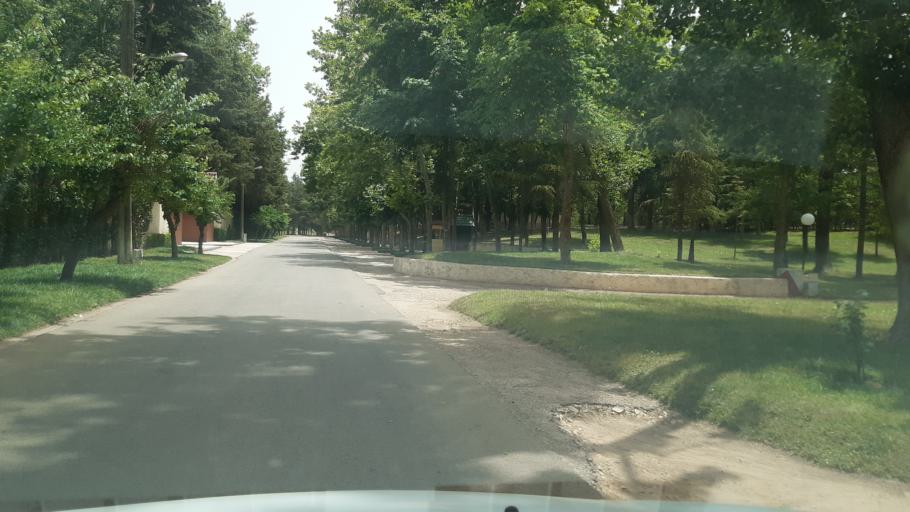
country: MA
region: Meknes-Tafilalet
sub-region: Ifrane
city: Ifrane
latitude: 33.6484
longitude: -5.0344
